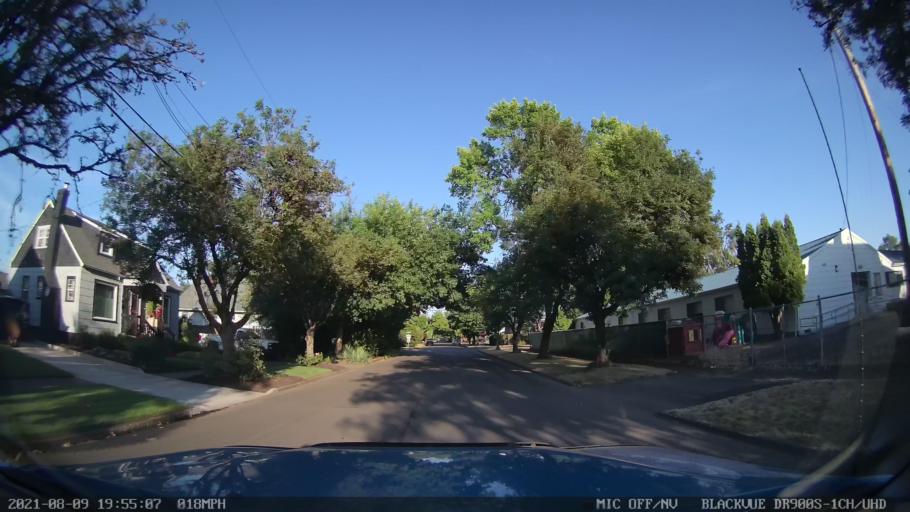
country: US
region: Oregon
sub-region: Marion County
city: Salem
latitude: 44.9539
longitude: -123.0236
